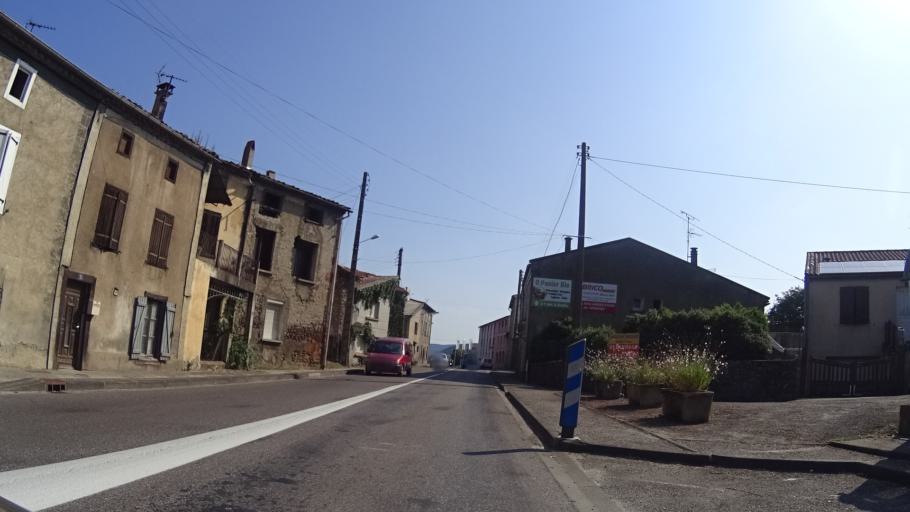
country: FR
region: Midi-Pyrenees
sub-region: Departement de l'Ariege
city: Lavelanet
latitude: 42.9194
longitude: 1.8305
